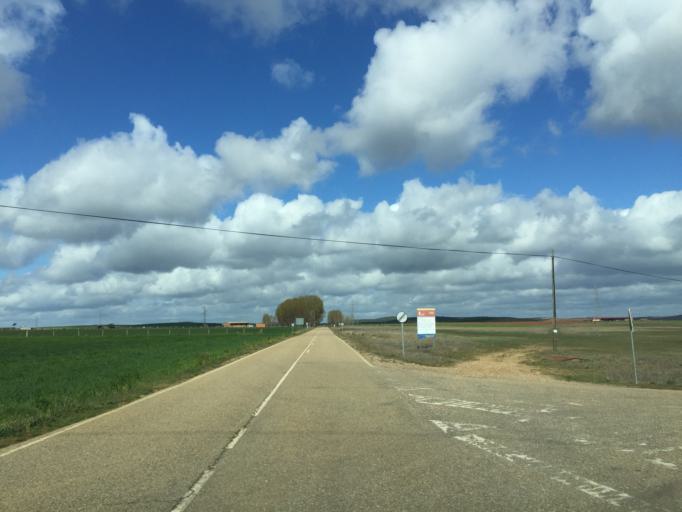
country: ES
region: Castille and Leon
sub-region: Provincia de Zamora
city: Palacios del Pan
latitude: 41.5774
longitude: -5.9246
